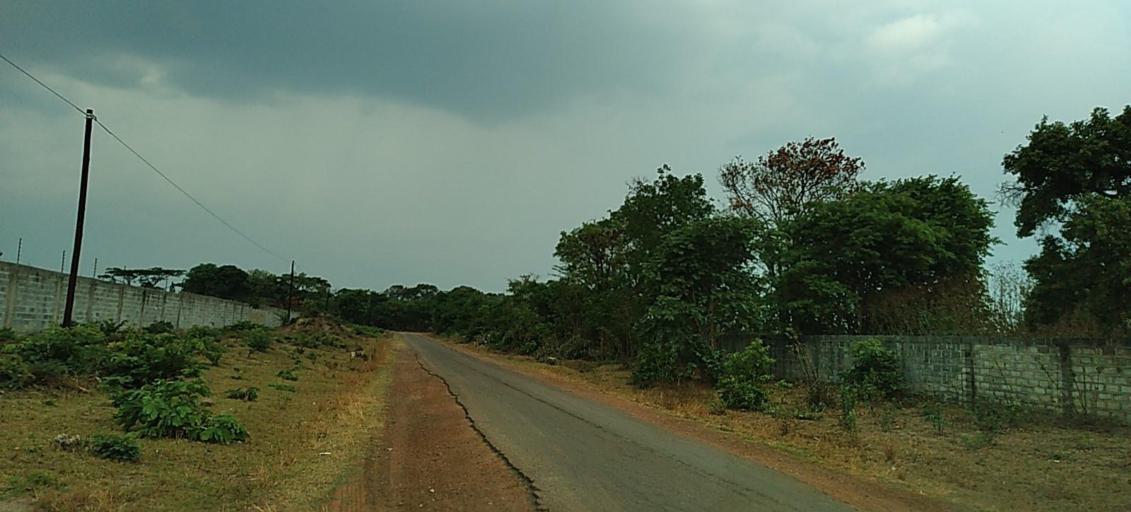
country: ZM
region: Copperbelt
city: Kalulushi
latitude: -12.8901
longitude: 28.1234
